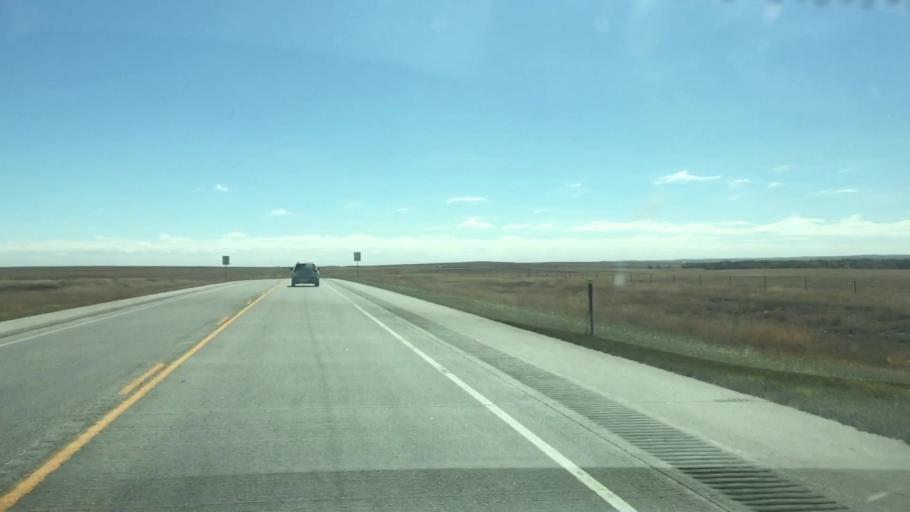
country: US
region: Colorado
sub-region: Lincoln County
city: Hugo
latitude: 39.1875
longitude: -103.5568
